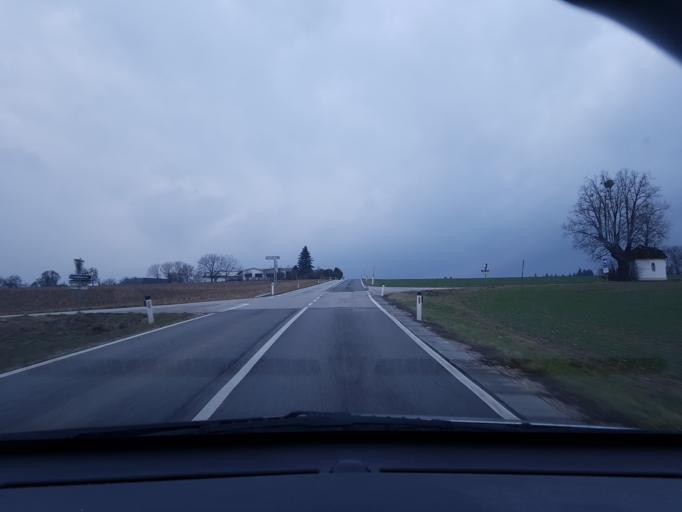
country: AT
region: Upper Austria
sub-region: Politischer Bezirk Steyr-Land
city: Sierning
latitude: 48.1193
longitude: 14.3478
